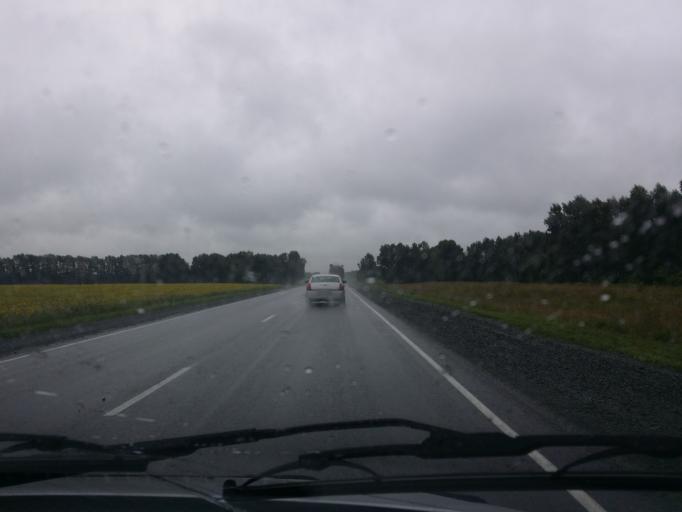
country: RU
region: Altai Krai
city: Bayunovskiye Klyuchi
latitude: 53.3145
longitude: 84.2209
